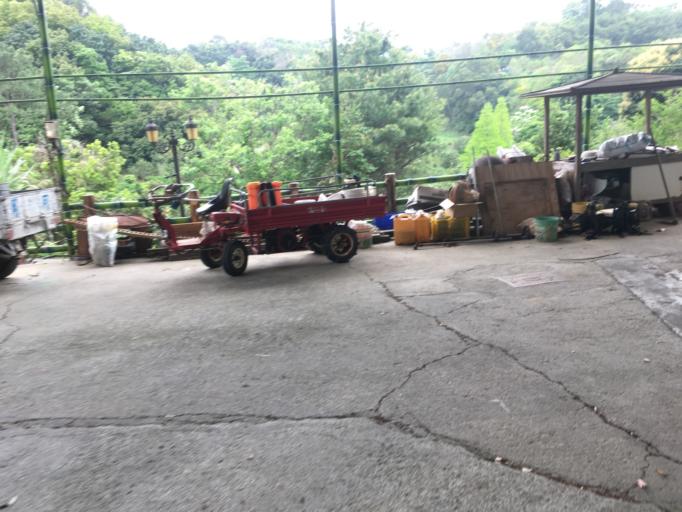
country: TW
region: Taiwan
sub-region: Hsinchu
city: Hsinchu
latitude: 24.7422
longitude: 120.9782
